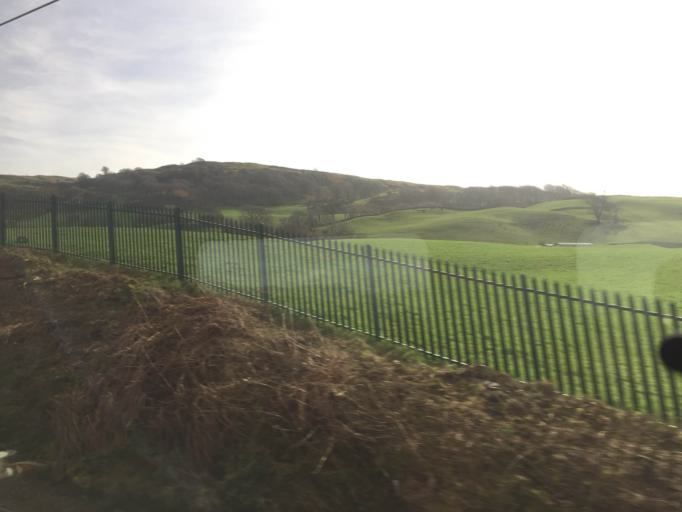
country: GB
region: England
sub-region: Cumbria
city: Kendal
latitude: 54.3409
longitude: -2.7138
